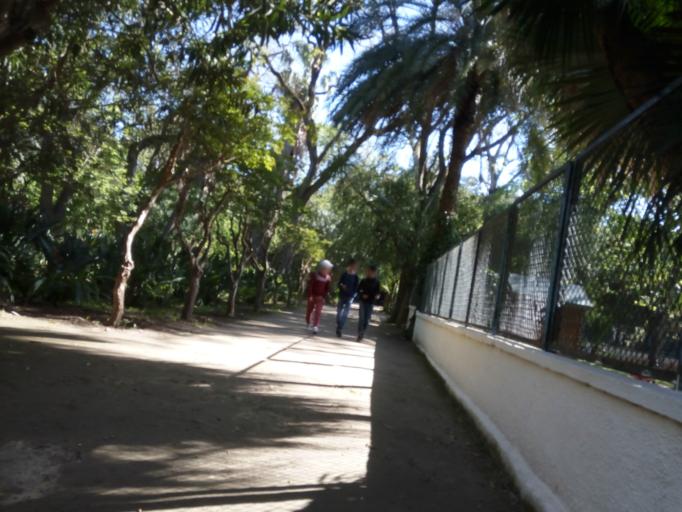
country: DZ
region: Alger
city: Algiers
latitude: 36.7482
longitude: 3.0783
